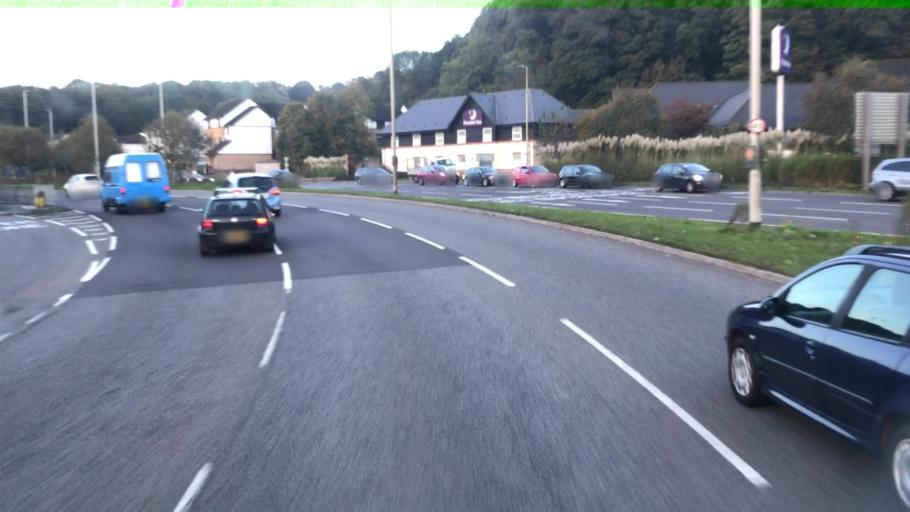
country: GB
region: England
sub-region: Devon
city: Plympton
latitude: 50.3905
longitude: -4.0876
